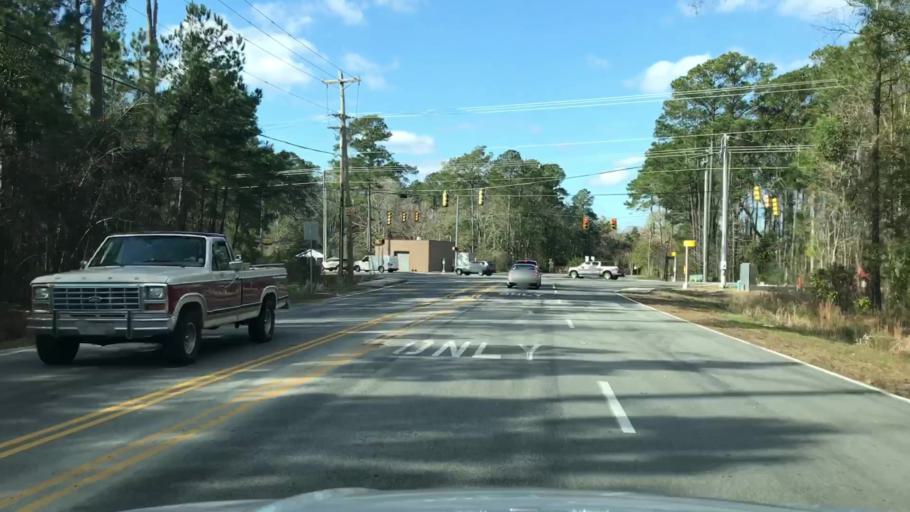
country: US
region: South Carolina
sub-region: Horry County
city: Socastee
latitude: 33.6600
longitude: -79.0119
